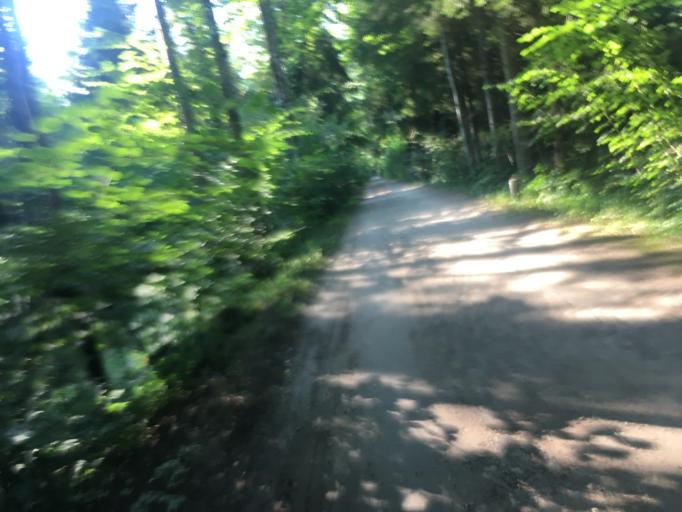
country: CH
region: Bern
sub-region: Emmental District
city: Oberburg
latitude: 47.0316
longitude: 7.6402
